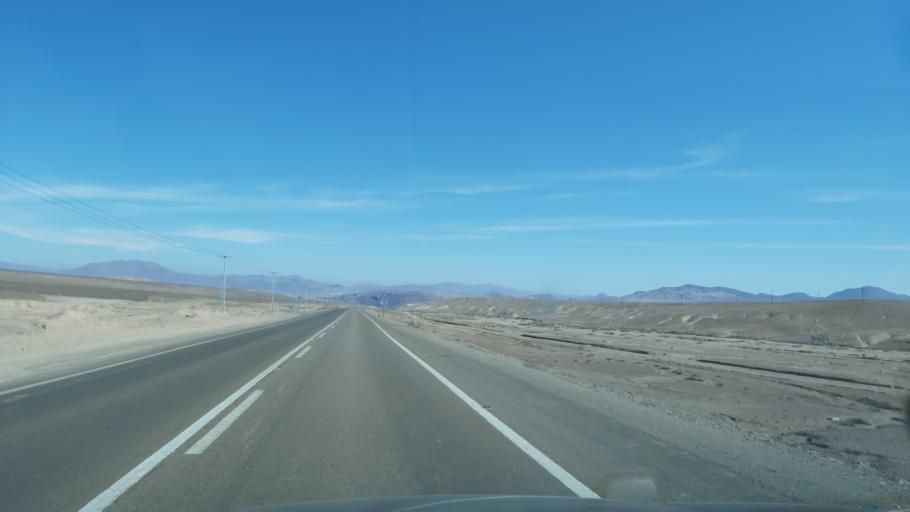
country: CL
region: Atacama
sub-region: Provincia de Chanaral
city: Diego de Almagro
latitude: -26.4337
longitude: -70.0065
